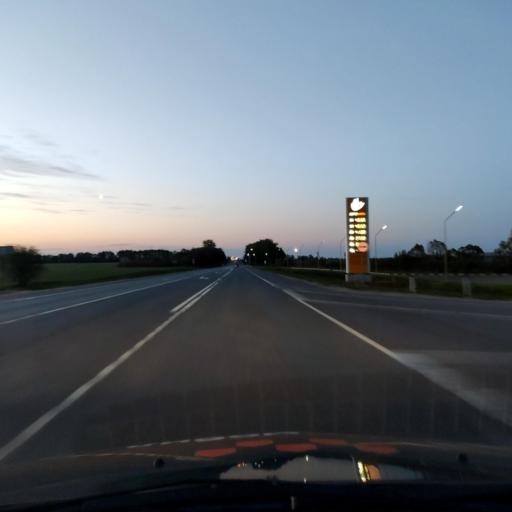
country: RU
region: Orjol
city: Zmiyevka
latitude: 52.7116
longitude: 36.3514
